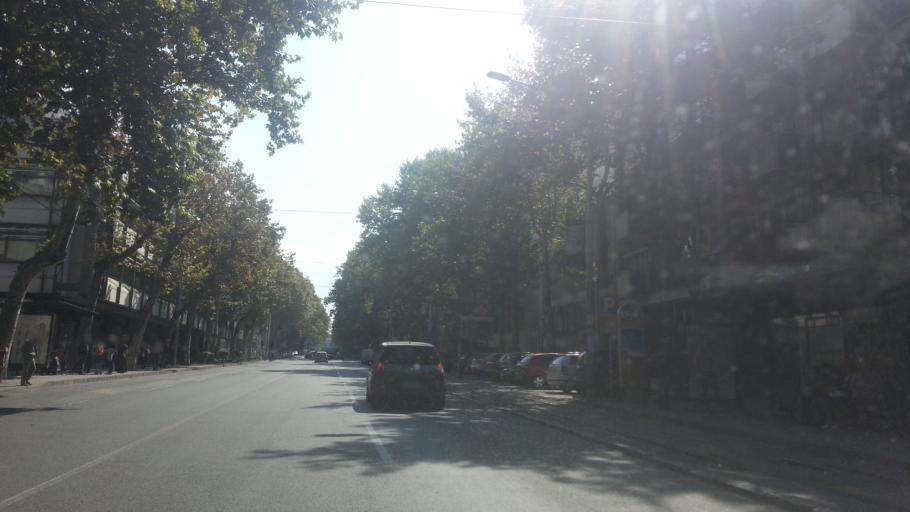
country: RS
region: Central Serbia
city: Belgrade
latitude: 44.8107
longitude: 20.4744
